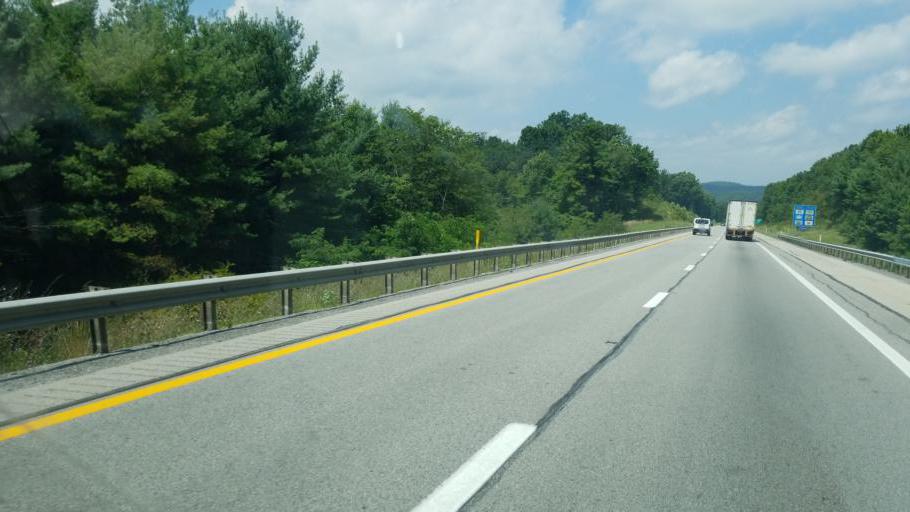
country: US
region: West Virginia
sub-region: Mercer County
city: Athens
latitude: 37.4143
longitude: -81.0623
